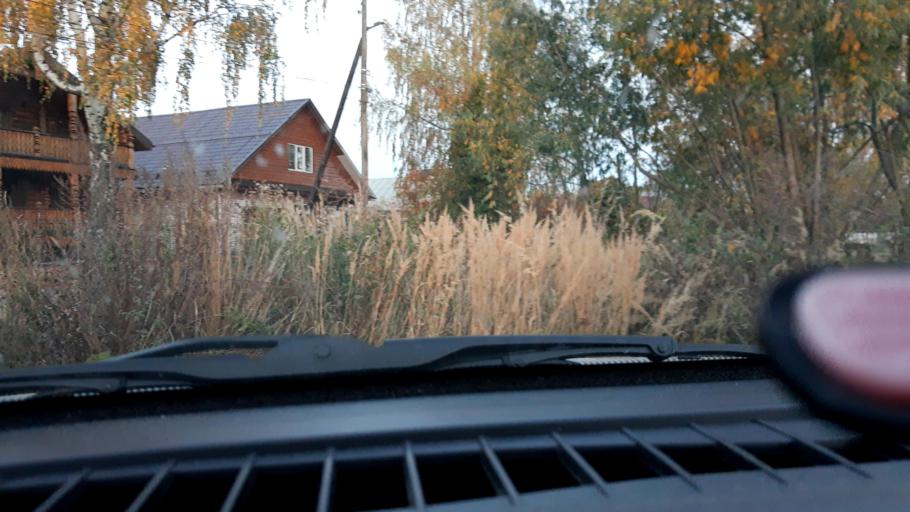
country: RU
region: Nizjnij Novgorod
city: Gorodets
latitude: 56.6352
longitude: 43.4697
